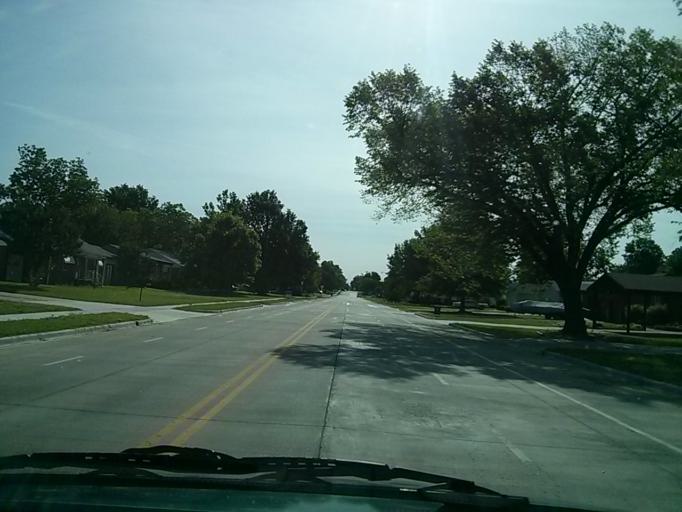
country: US
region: Oklahoma
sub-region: Tulsa County
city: Tulsa
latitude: 36.1551
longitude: -95.9111
